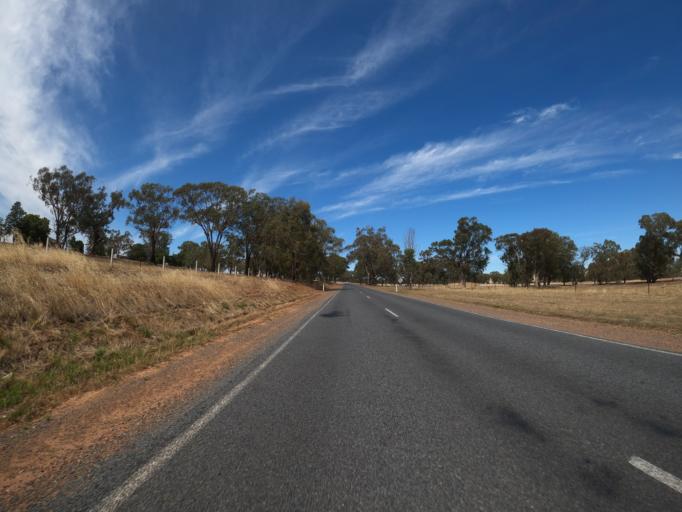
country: AU
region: Victoria
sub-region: Benalla
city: Benalla
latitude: -36.3322
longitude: 145.9607
